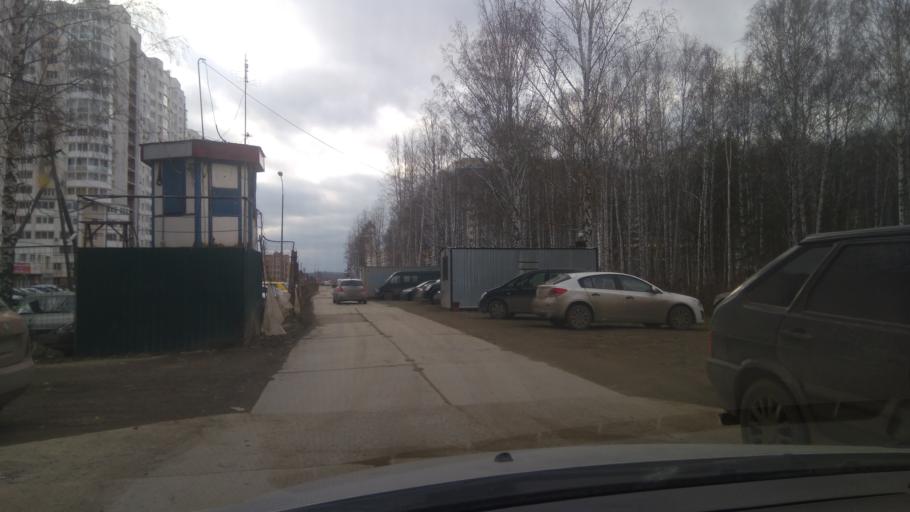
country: RU
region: Sverdlovsk
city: Sovkhoznyy
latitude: 56.7854
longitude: 60.5437
